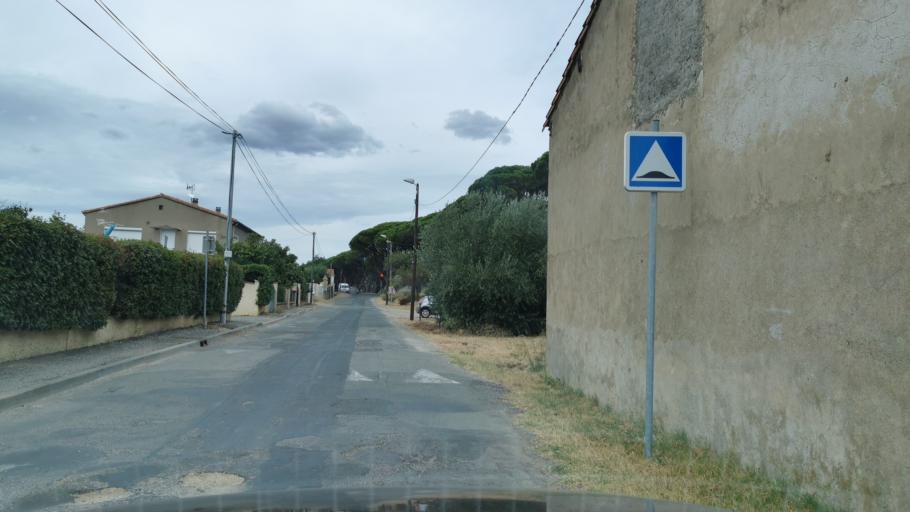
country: FR
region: Languedoc-Roussillon
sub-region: Departement de l'Aude
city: Saint-Marcel-sur-Aude
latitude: 43.2641
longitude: 2.9421
